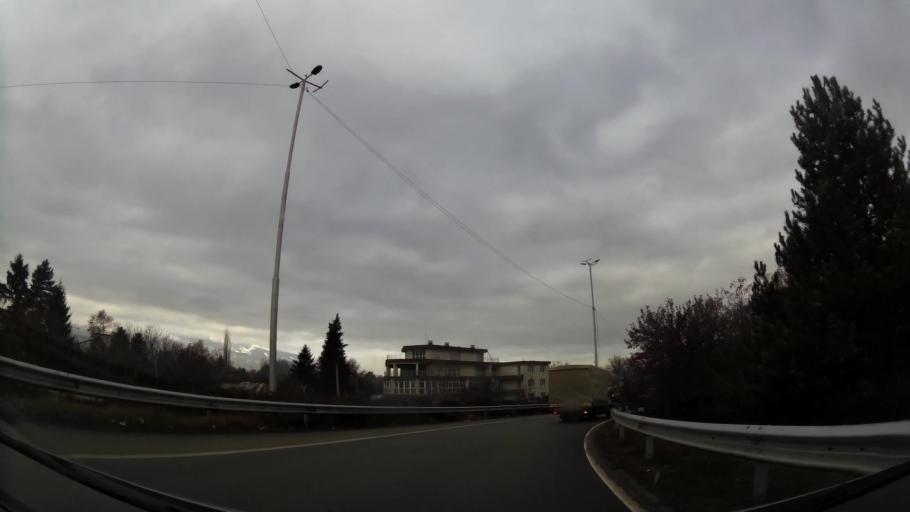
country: BG
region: Sofia-Capital
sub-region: Stolichna Obshtina
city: Sofia
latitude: 42.6321
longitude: 23.4467
